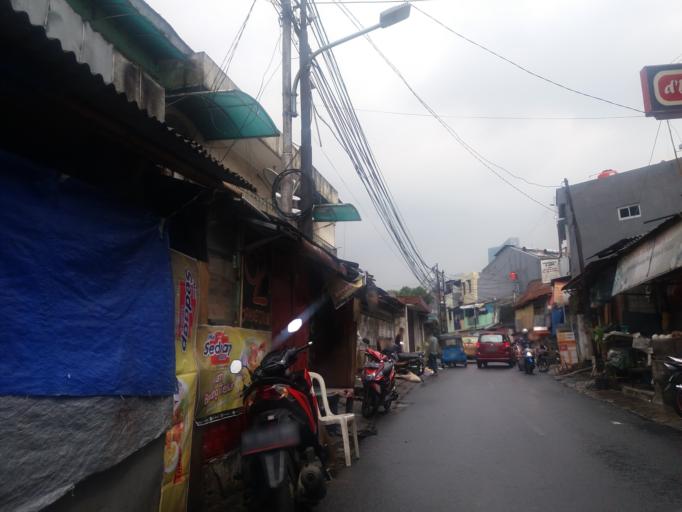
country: ID
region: Jakarta Raya
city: Jakarta
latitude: -6.2142
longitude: 106.8260
